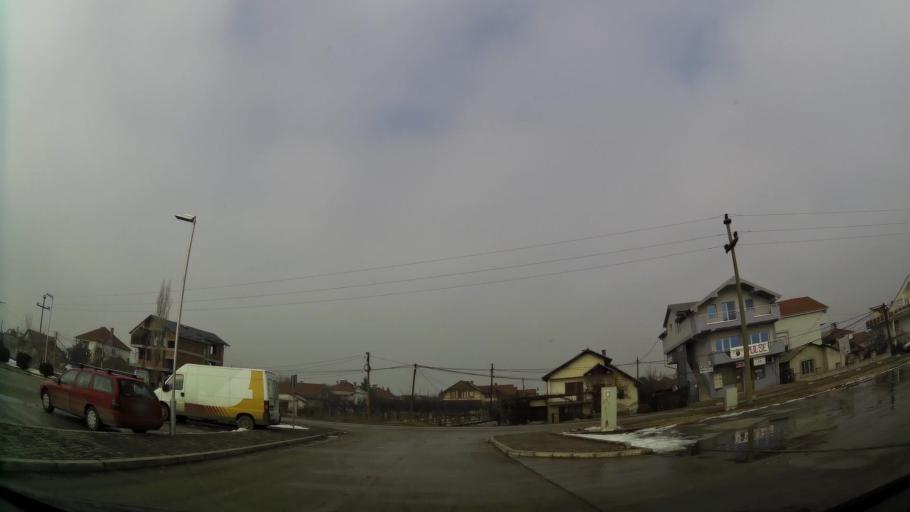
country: MK
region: Ilinden
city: Ilinden
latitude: 41.9910
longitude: 21.5833
